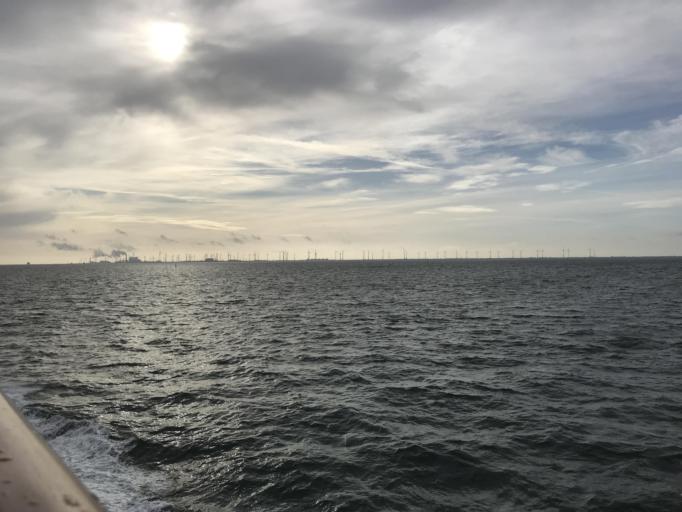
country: DE
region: Lower Saxony
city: Borkum
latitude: 53.5253
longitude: 6.7671
